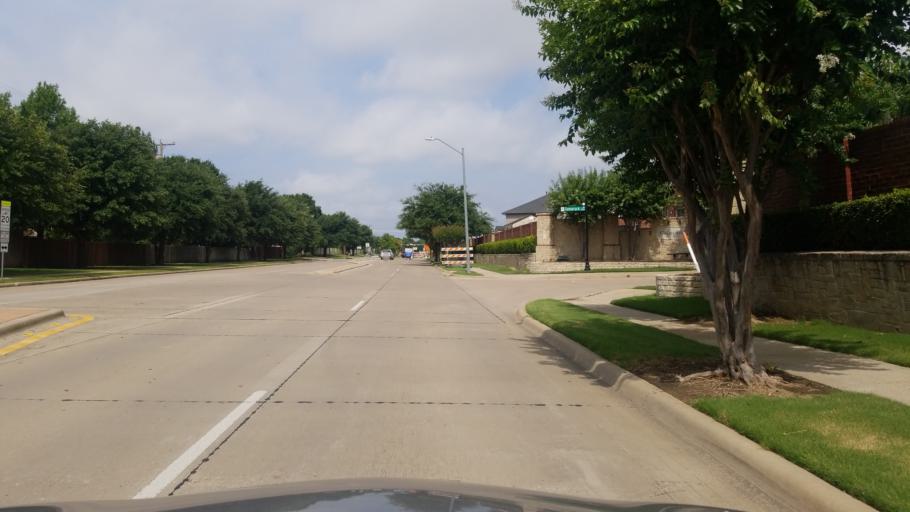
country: US
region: Texas
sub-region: Dallas County
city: Grand Prairie
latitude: 32.6841
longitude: -97.0405
